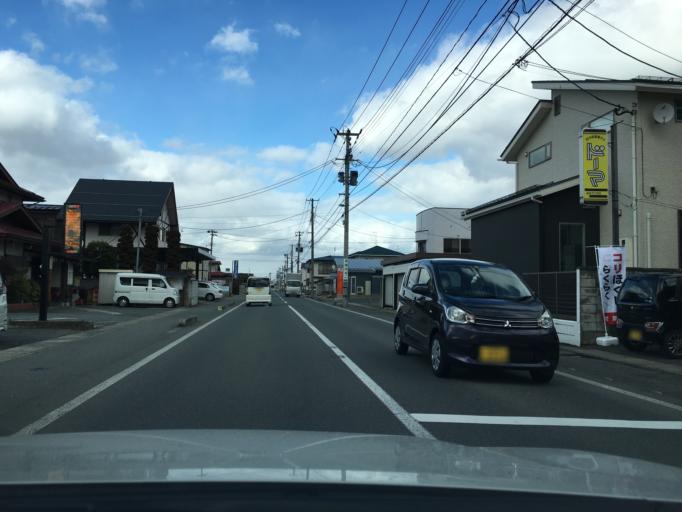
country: JP
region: Yamagata
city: Yamagata-shi
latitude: 38.2477
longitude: 140.3134
